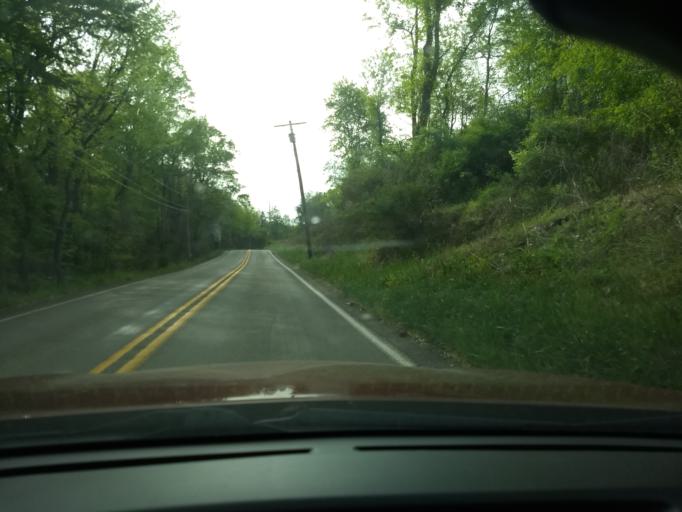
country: US
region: Pennsylvania
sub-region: Allegheny County
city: Bakerstown
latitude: 40.6036
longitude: -79.9041
